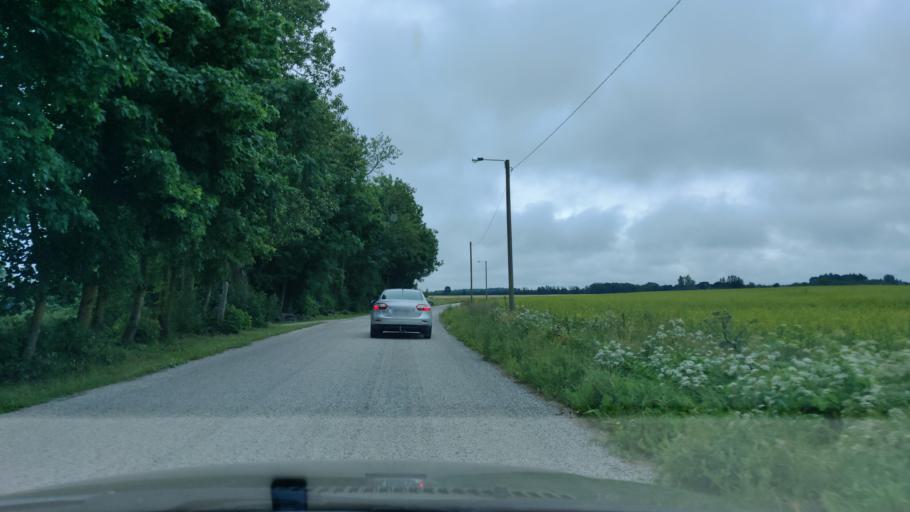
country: EE
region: Jaervamaa
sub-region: Jaerva-Jaani vald
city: Jarva-Jaani
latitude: 59.0943
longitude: 25.6992
